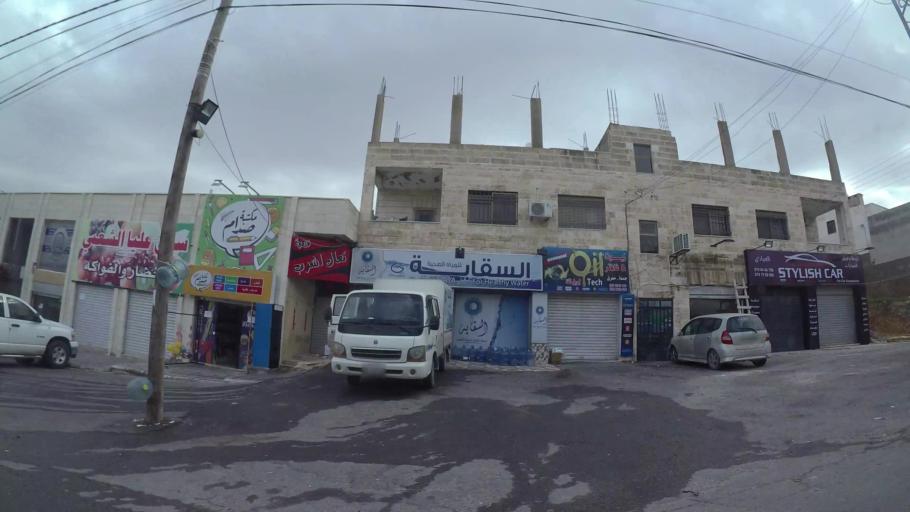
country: JO
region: Amman
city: Umm as Summaq
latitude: 31.9060
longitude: 35.8473
